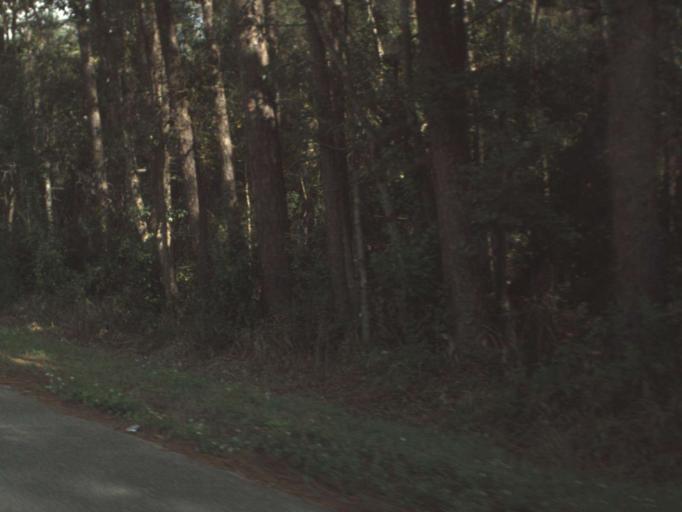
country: US
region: Florida
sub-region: Calhoun County
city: Blountstown
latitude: 30.4578
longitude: -85.0635
